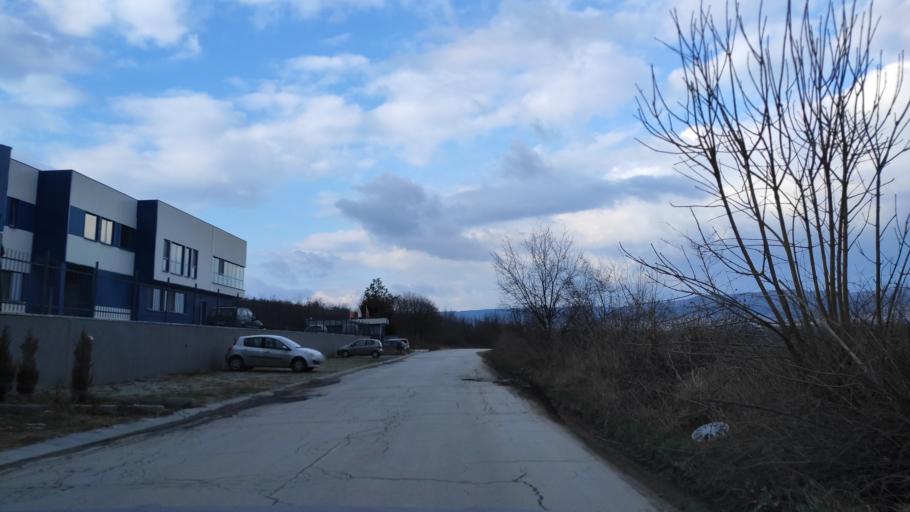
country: BG
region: Varna
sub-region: Obshtina Aksakovo
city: Aksakovo
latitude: 43.2258
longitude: 27.8049
